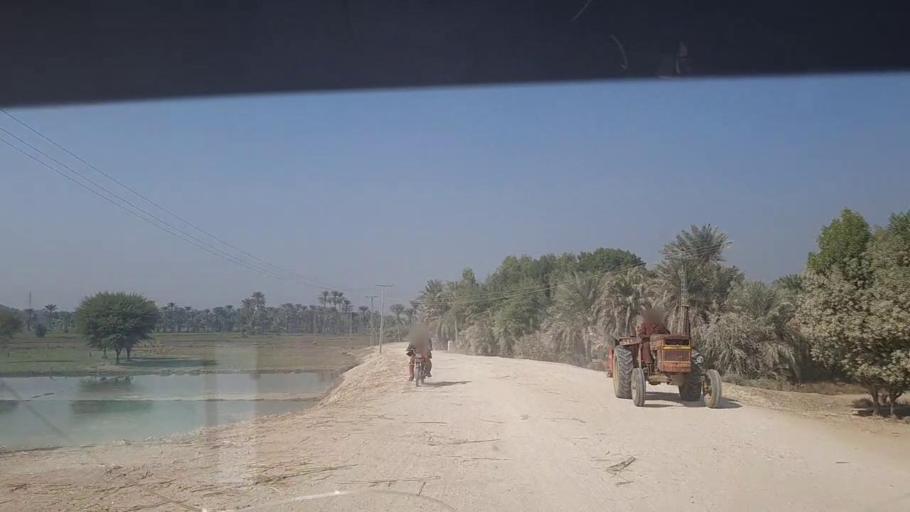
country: PK
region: Sindh
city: Kot Diji
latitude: 27.3591
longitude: 68.7096
